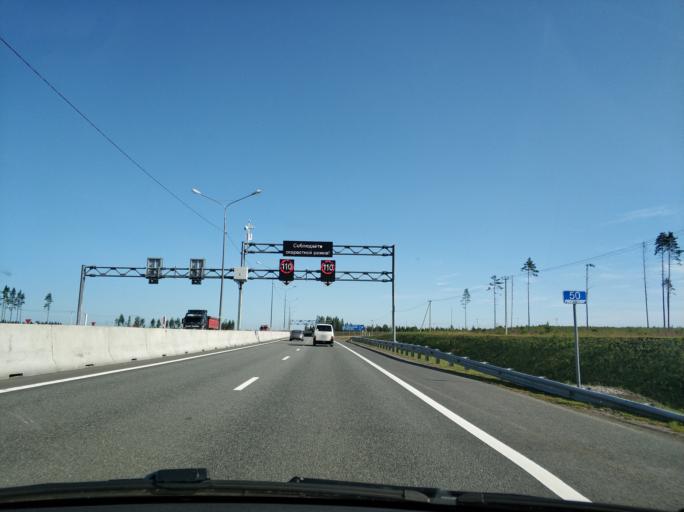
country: RU
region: Leningrad
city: Sosnovo
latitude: 60.4976
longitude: 30.1957
